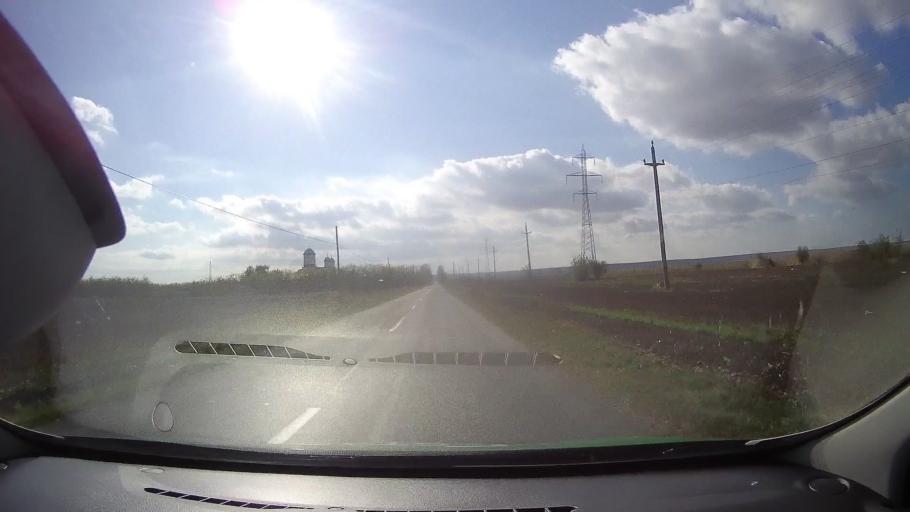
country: RO
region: Constanta
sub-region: Comuna Istria
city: Istria
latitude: 44.5475
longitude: 28.6934
